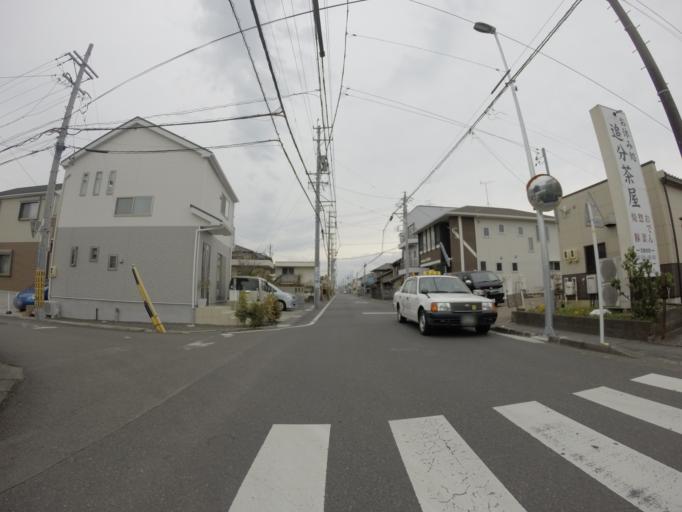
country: JP
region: Shizuoka
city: Shizuoka-shi
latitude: 35.0141
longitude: 138.4708
